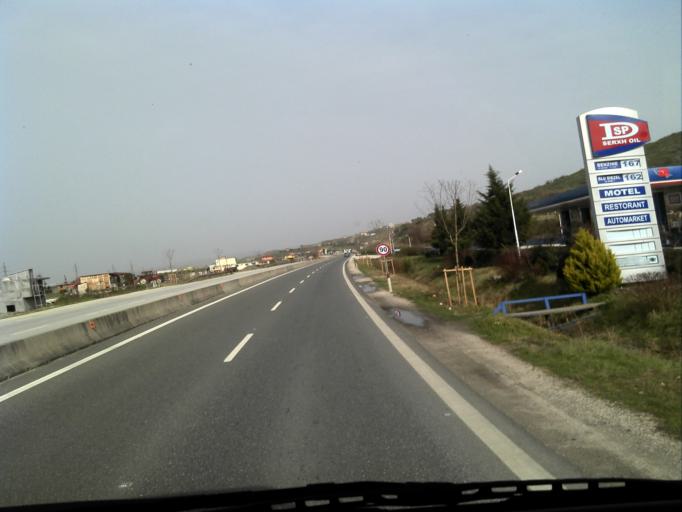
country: AL
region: Fier
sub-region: Rrethi i Lushnjes
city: Golem
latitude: 41.0088
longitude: 19.6633
